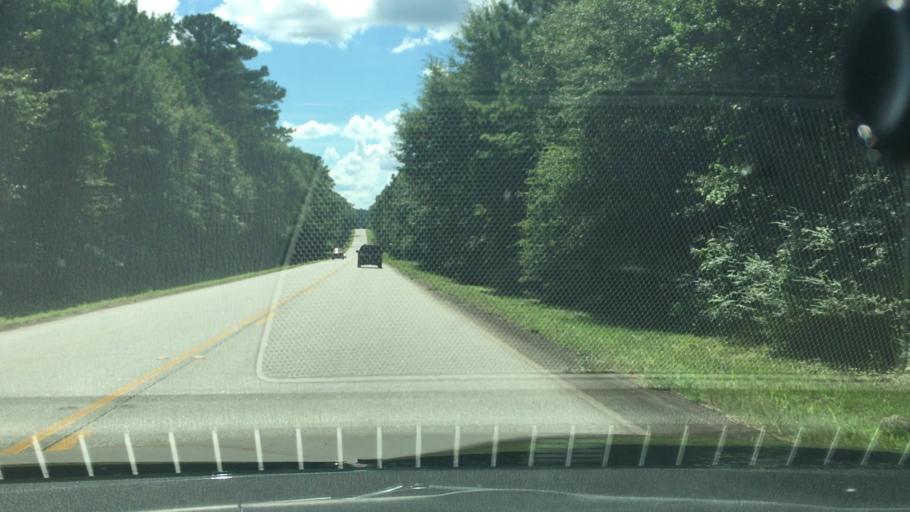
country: US
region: Georgia
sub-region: Jasper County
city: Monticello
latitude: 33.3035
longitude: -83.6262
